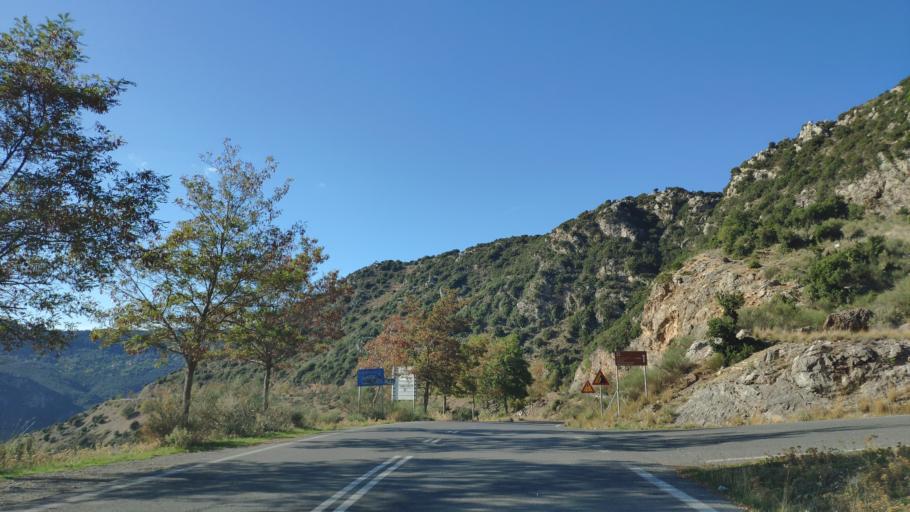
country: GR
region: Peloponnese
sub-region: Nomos Arkadias
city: Dimitsana
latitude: 37.5810
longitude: 22.0568
